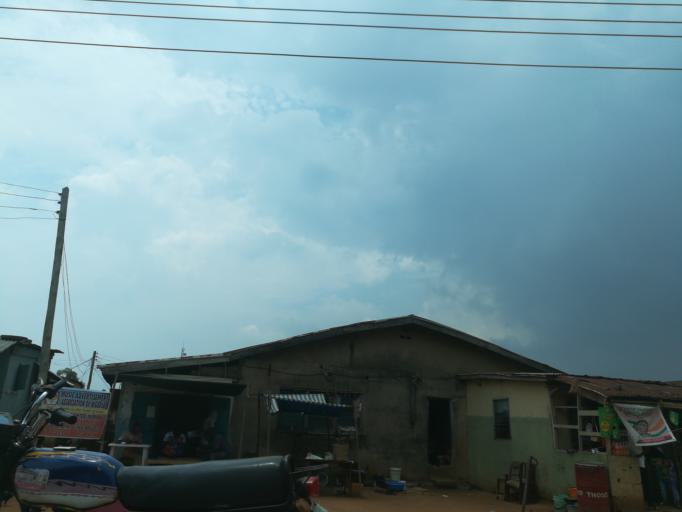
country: NG
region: Lagos
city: Ikorodu
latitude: 6.5656
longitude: 3.5914
